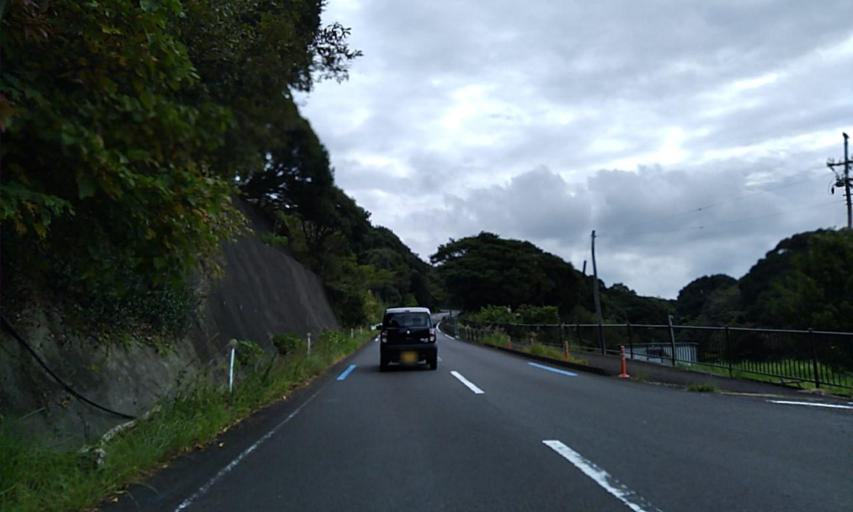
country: JP
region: Wakayama
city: Shingu
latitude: 33.4683
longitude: 135.8255
